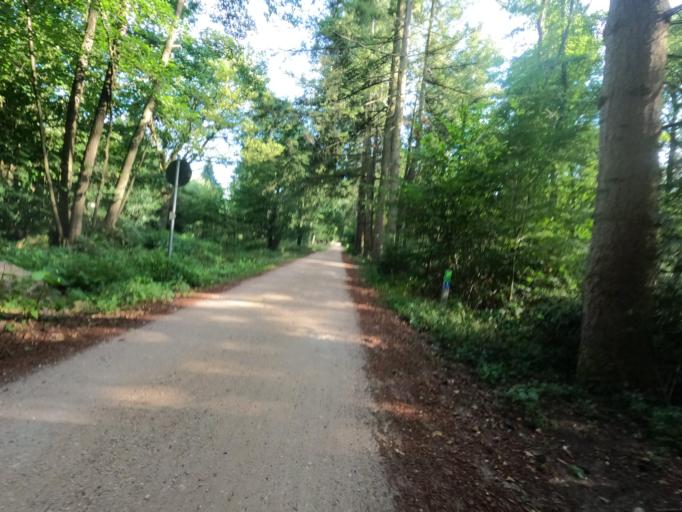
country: NL
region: Limburg
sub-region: Gemeente Beesel
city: Offenbeek
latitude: 51.2291
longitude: 6.0884
